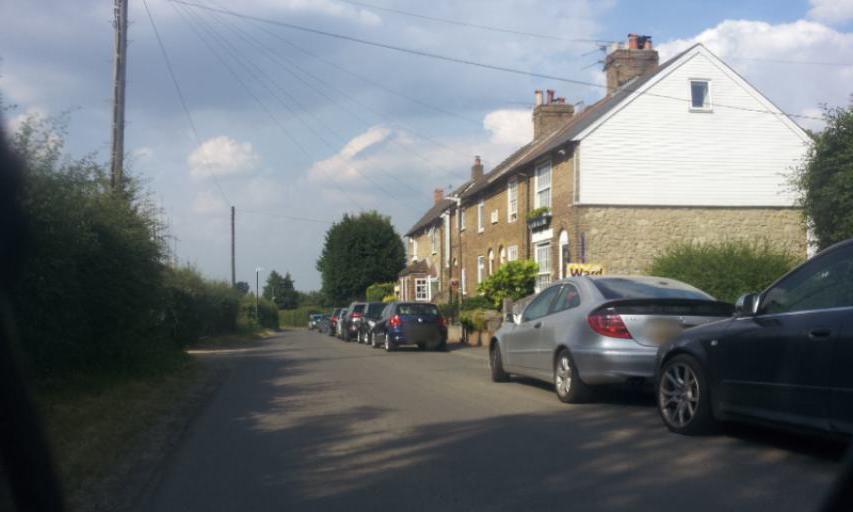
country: GB
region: England
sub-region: Kent
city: Maidstone
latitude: 51.2370
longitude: 0.4969
